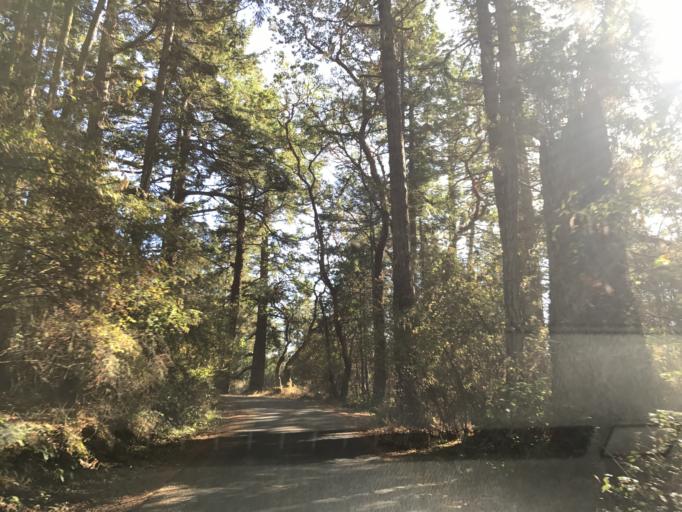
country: US
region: Washington
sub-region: Skagit County
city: Anacortes
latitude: 48.4938
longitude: -122.7004
